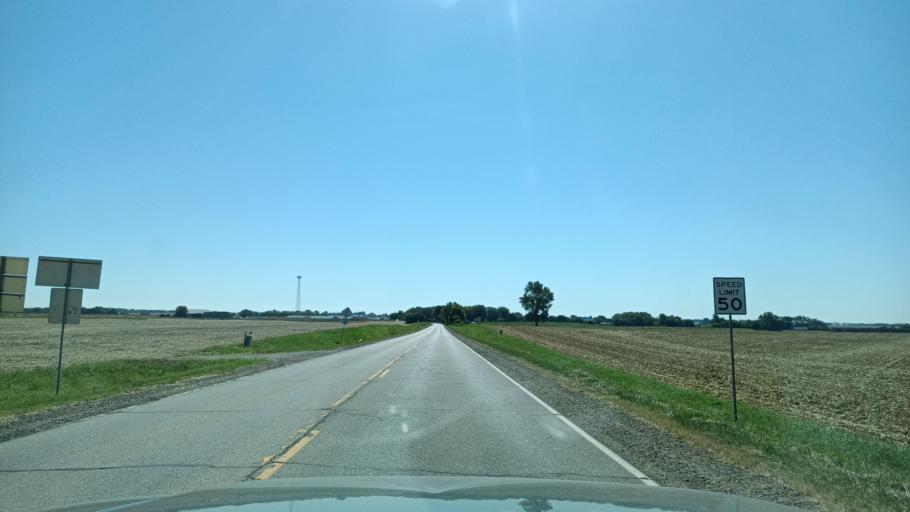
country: US
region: Illinois
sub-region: Peoria County
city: Elmwood
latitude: 40.8374
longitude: -89.8781
